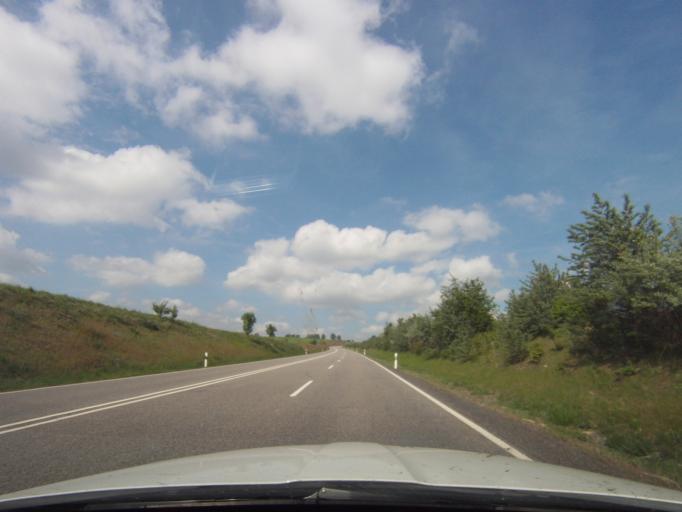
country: DE
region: Thuringia
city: Miesitz
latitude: 50.7423
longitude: 11.8439
